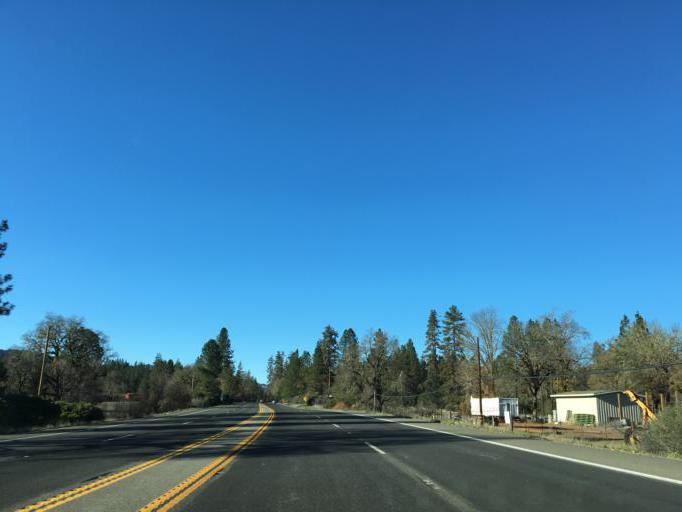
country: US
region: California
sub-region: Mendocino County
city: Laytonville
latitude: 39.7288
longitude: -123.5060
